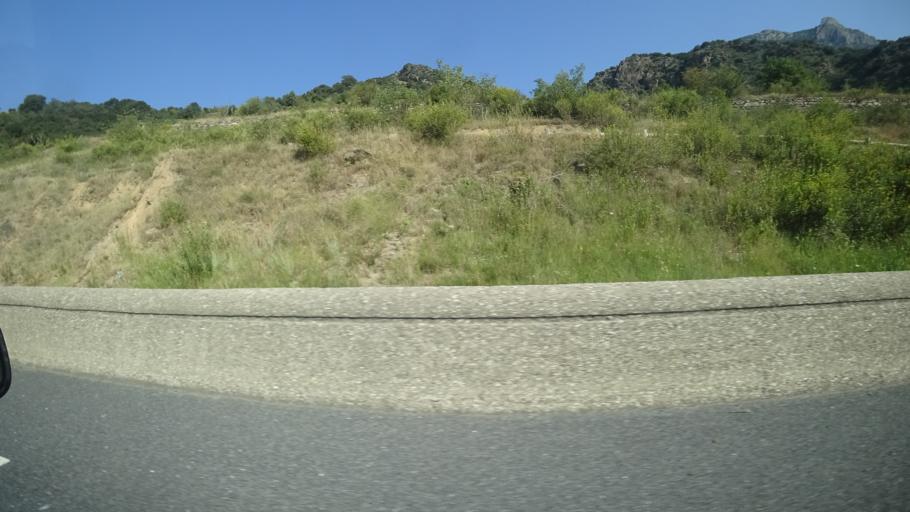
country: FR
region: Languedoc-Roussillon
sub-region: Departement des Pyrenees-Orientales
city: Vernet-les-Bains
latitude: 42.5730
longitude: 2.3379
